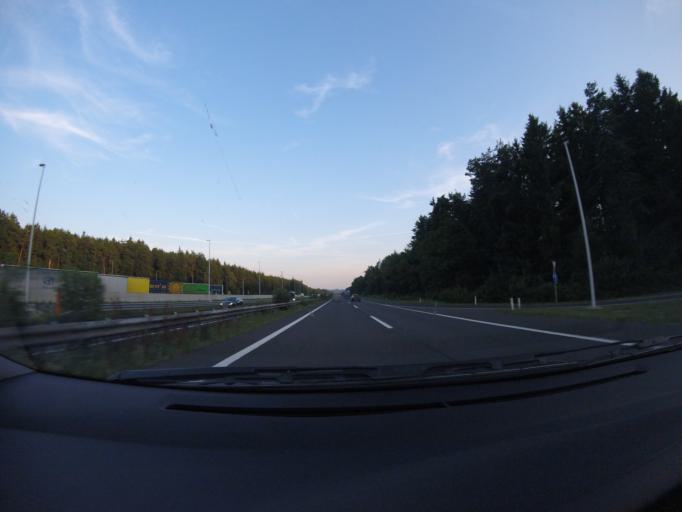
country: AT
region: Styria
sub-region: Politischer Bezirk Hartberg-Fuerstenfeld
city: Hainersdorf
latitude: 47.1171
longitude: 15.9843
